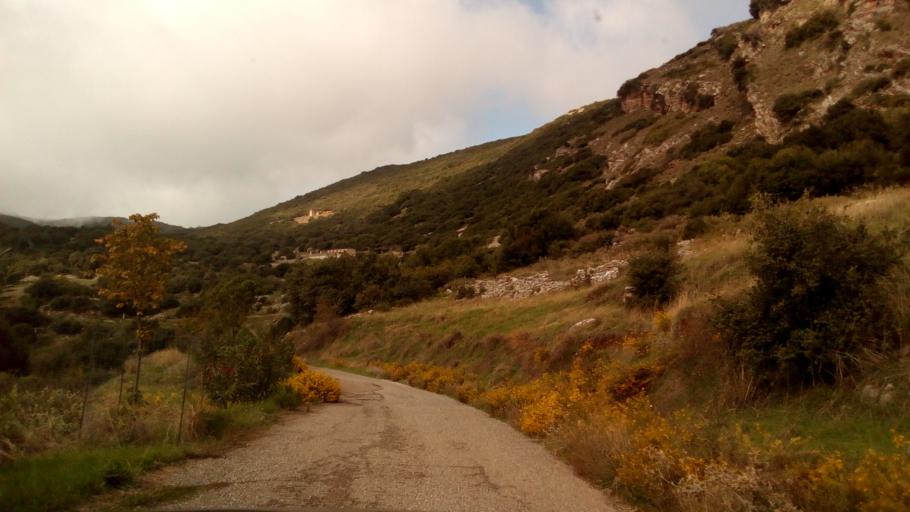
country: GR
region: West Greece
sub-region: Nomos Achaias
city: Kamarai
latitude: 38.4529
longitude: 21.9715
